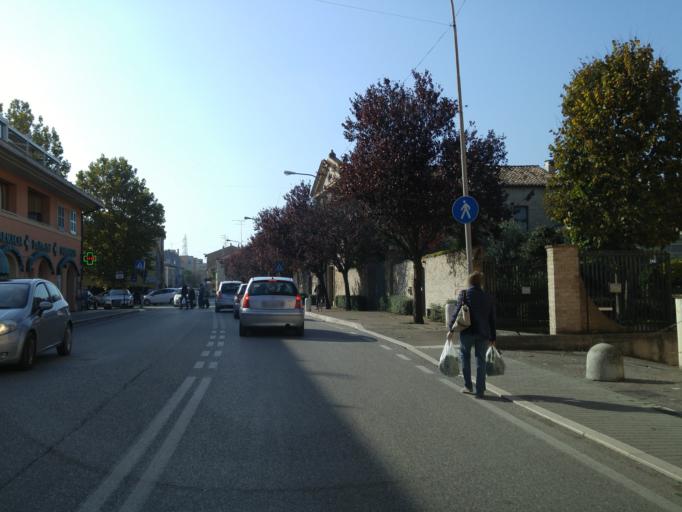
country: IT
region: The Marches
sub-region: Provincia di Pesaro e Urbino
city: Fano
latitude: 43.8384
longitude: 13.0200
